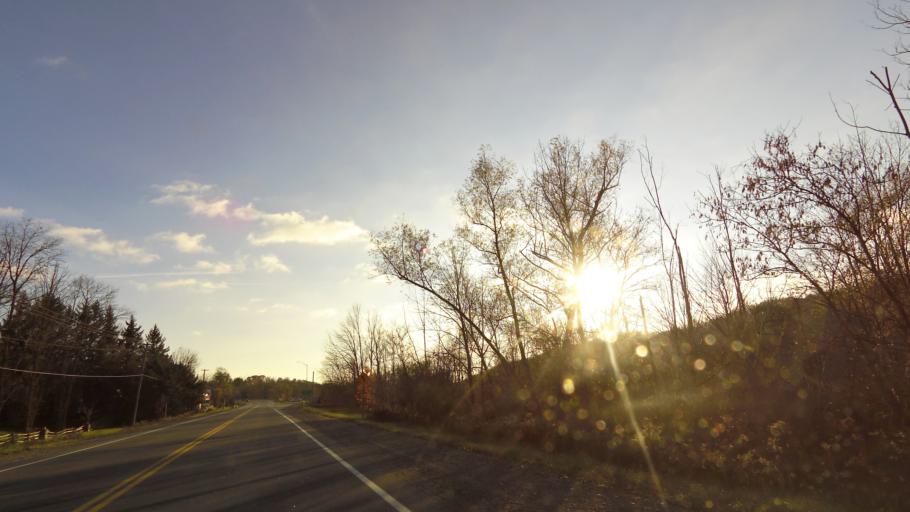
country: CA
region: Ontario
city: Cambridge
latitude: 43.3002
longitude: -80.3115
